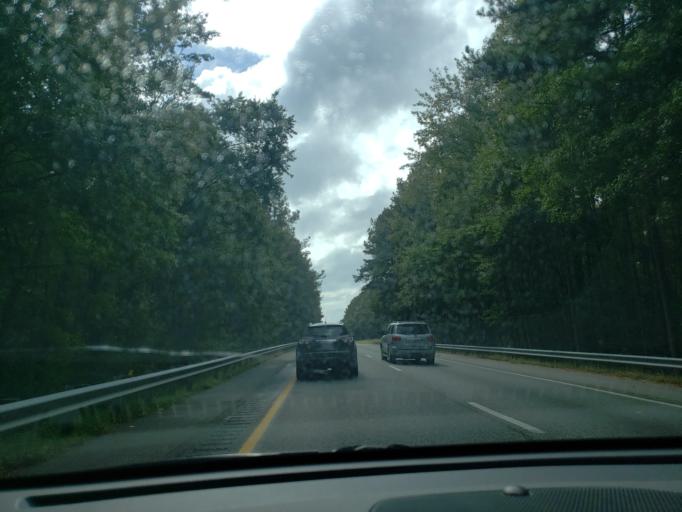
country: US
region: Virginia
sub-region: Brunswick County
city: Lawrenceville
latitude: 36.8942
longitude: -77.8032
